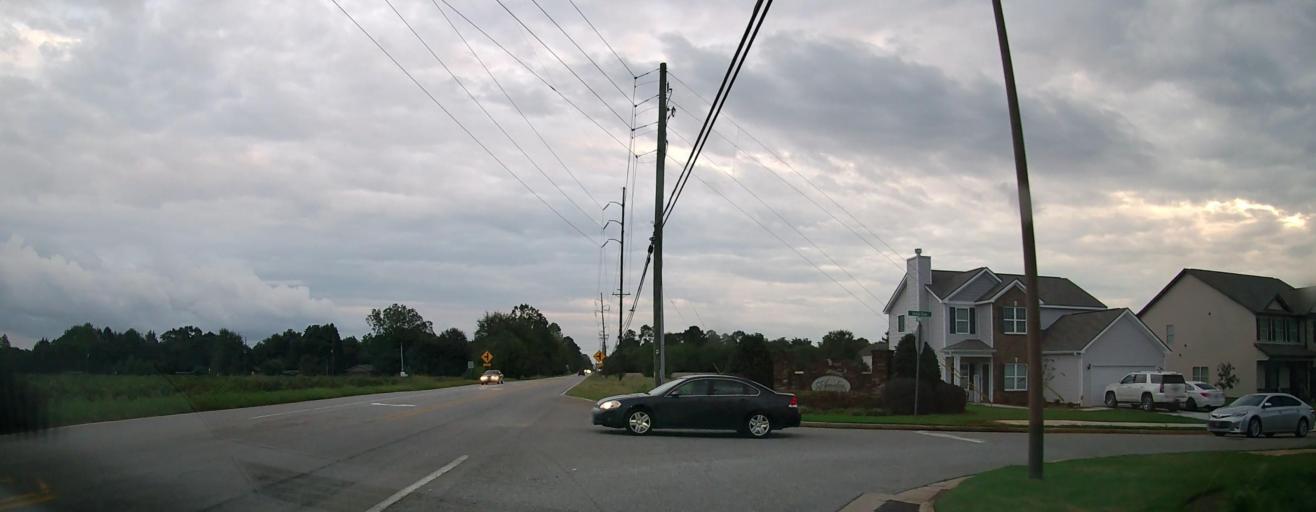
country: US
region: Georgia
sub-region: Houston County
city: Centerville
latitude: 32.6448
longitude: -83.7082
